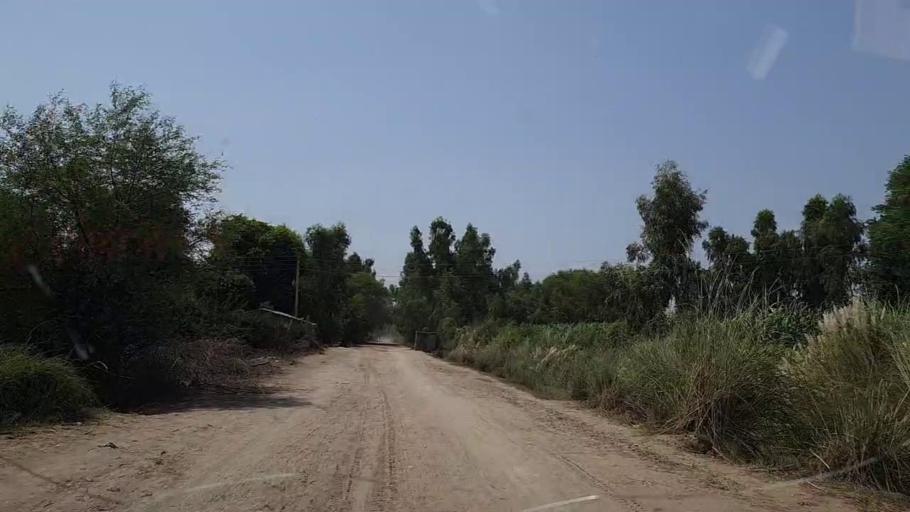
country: PK
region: Sindh
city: Ghotki
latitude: 28.0889
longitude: 69.3347
